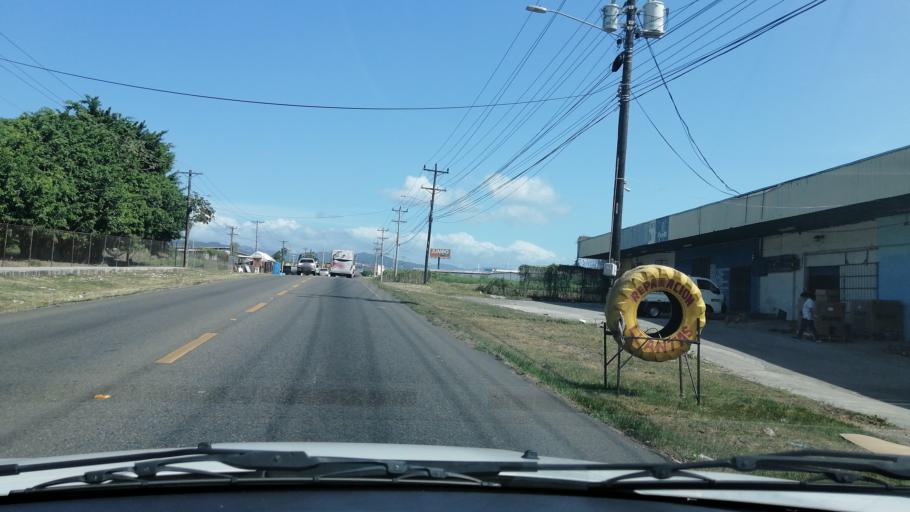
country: PA
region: Panama
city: Tocumen
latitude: 9.0748
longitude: -79.4122
